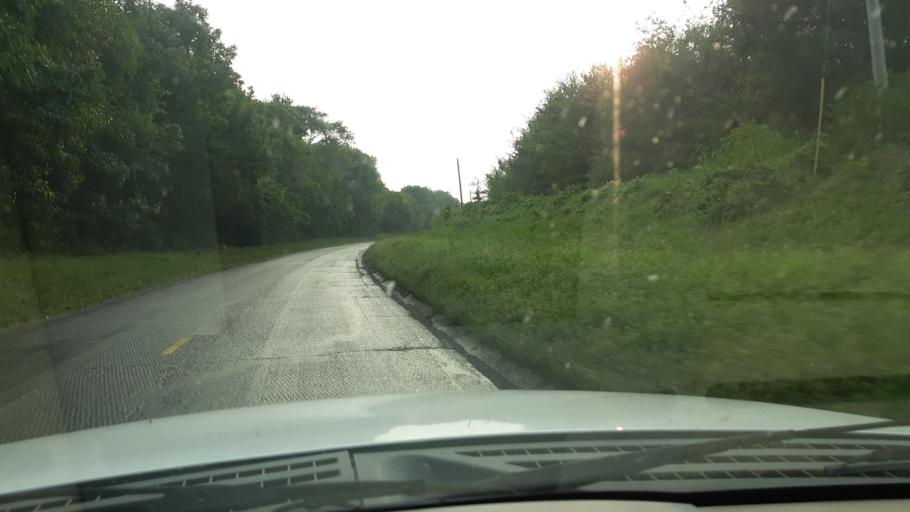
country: US
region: Illinois
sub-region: Edwards County
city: Grayville
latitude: 38.2968
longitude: -87.9567
